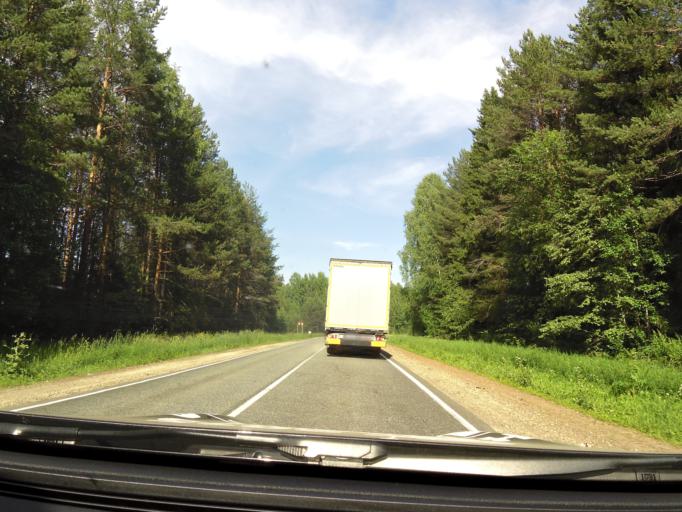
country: RU
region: Kirov
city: Belaya Kholunitsa
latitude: 58.8284
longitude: 50.6329
